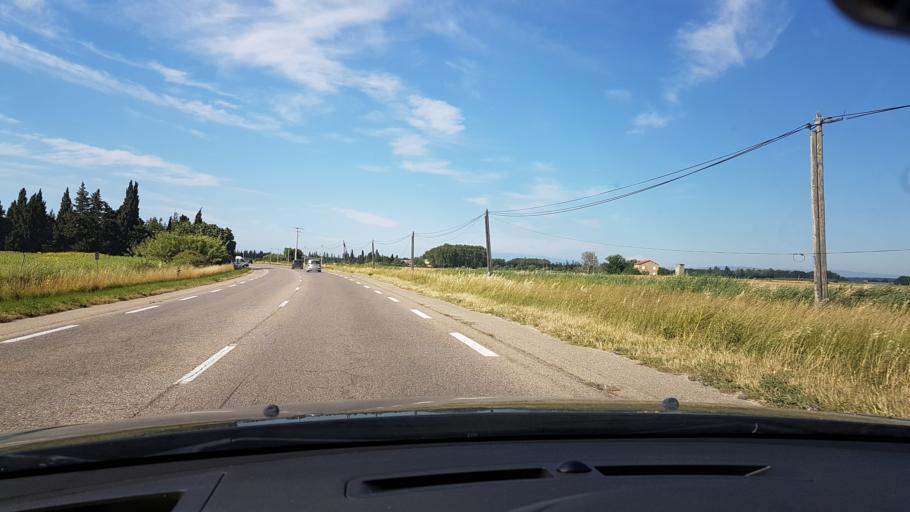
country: FR
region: Provence-Alpes-Cote d'Azur
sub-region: Departement des Bouches-du-Rhone
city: Saint-Etienne-du-Gres
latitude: 43.8099
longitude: 4.7247
